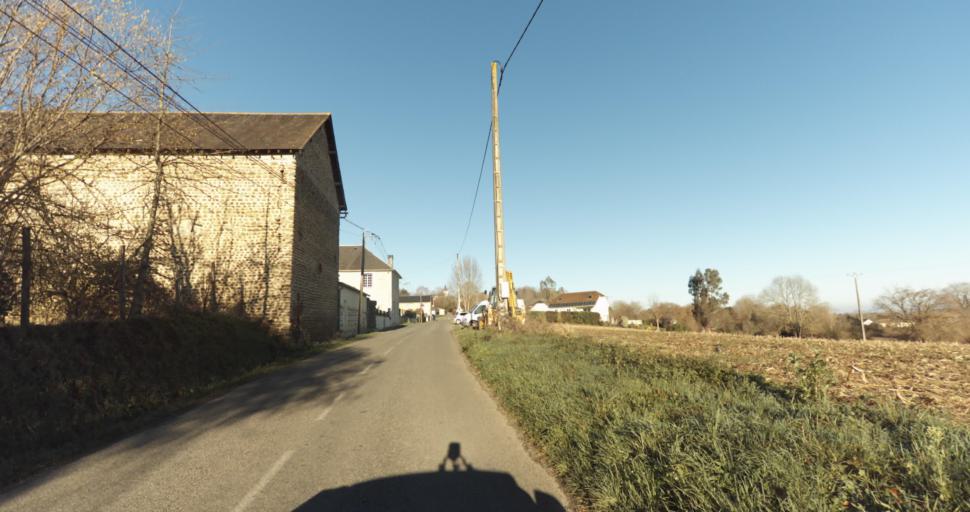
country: FR
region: Aquitaine
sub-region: Departement des Pyrenees-Atlantiques
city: Morlaas
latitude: 43.3234
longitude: -0.2543
